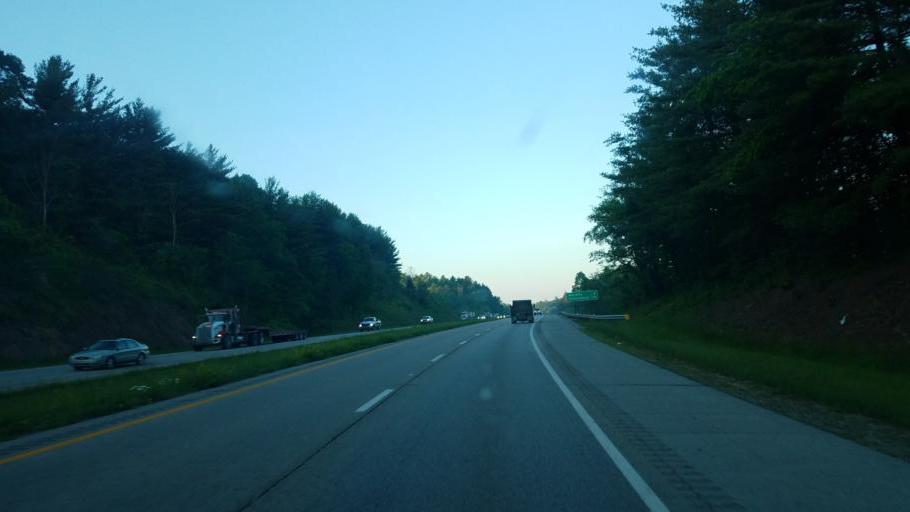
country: US
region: Ohio
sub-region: Washington County
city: Devola
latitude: 39.4661
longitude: -81.4358
